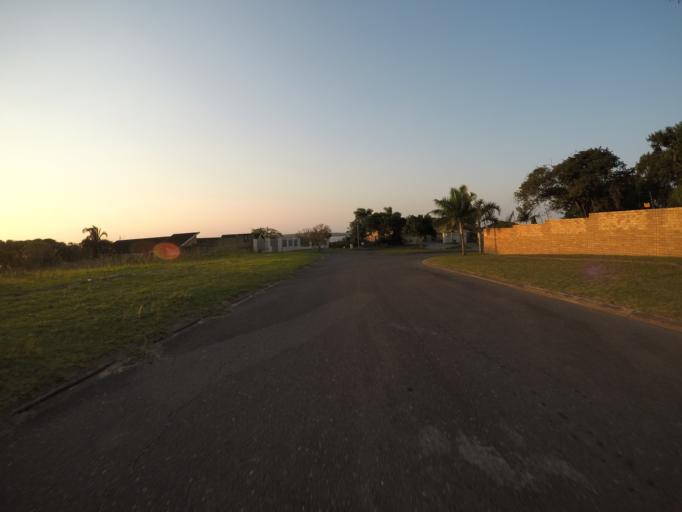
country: ZA
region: KwaZulu-Natal
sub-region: uThungulu District Municipality
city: Richards Bay
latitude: -28.7640
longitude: 32.1160
